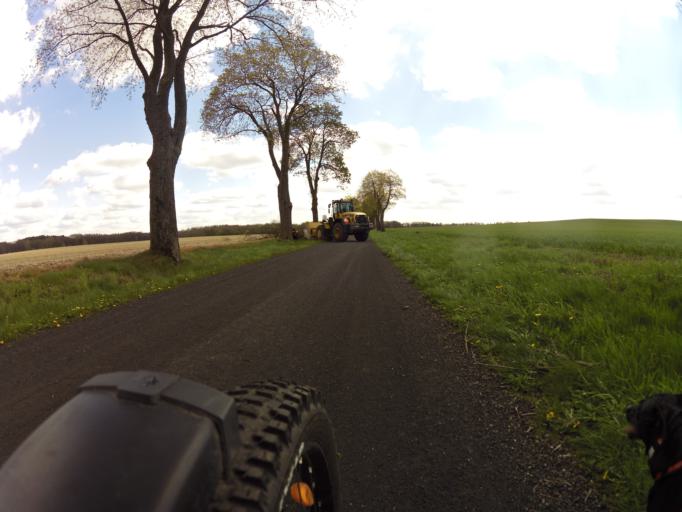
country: PL
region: West Pomeranian Voivodeship
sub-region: Powiat gryficki
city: Gryfice
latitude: 53.8530
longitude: 15.1688
